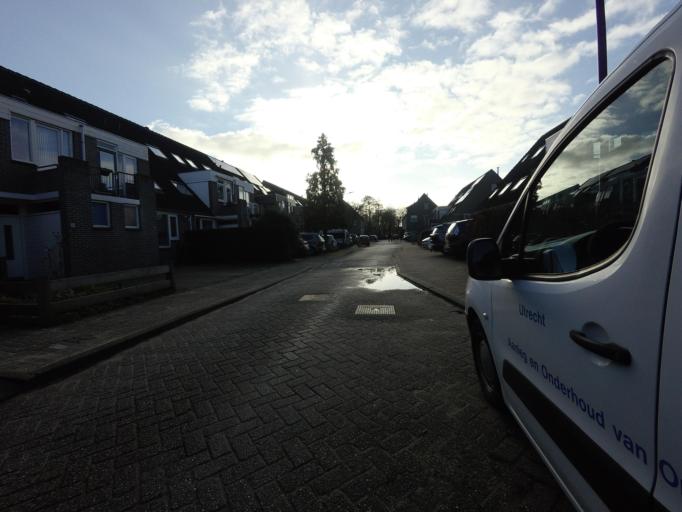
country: NL
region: Utrecht
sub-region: Gemeente Nieuwegein
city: Nieuwegein
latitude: 52.0356
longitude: 5.0685
